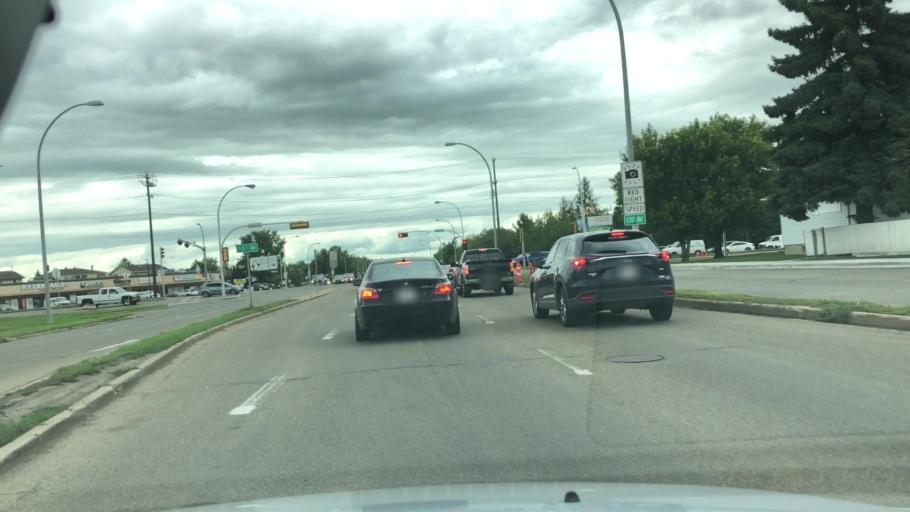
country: CA
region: Alberta
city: Edmonton
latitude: 53.5987
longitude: -113.5167
